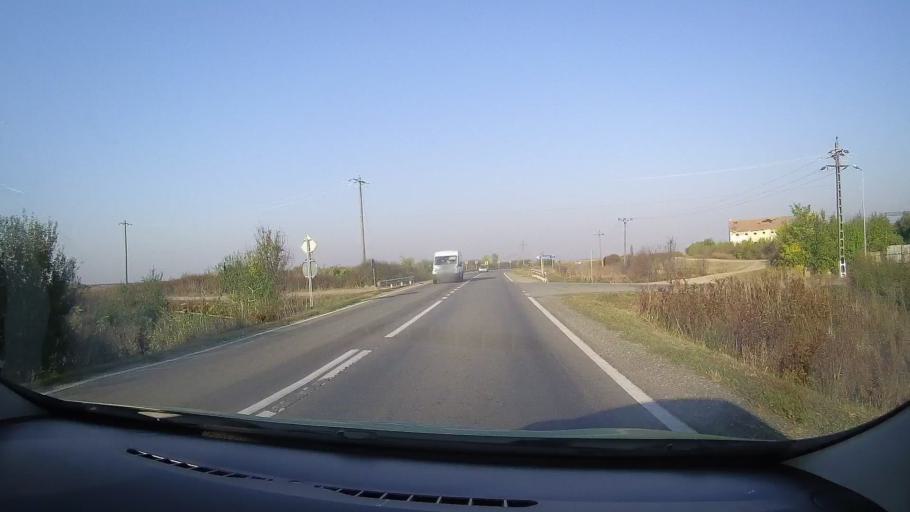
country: RO
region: Arad
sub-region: Comuna Socodor
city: Socodor
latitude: 46.5021
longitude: 21.4242
